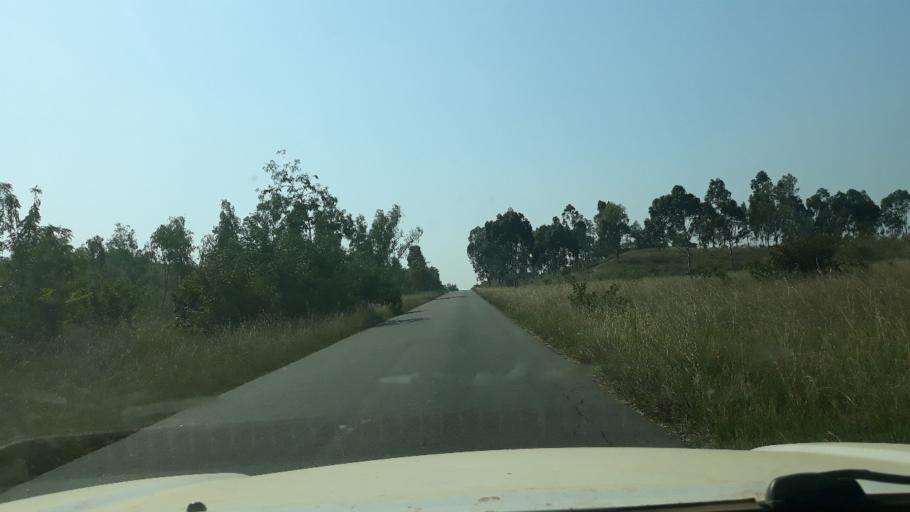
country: CD
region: South Kivu
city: Uvira
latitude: -3.1977
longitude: 29.1550
